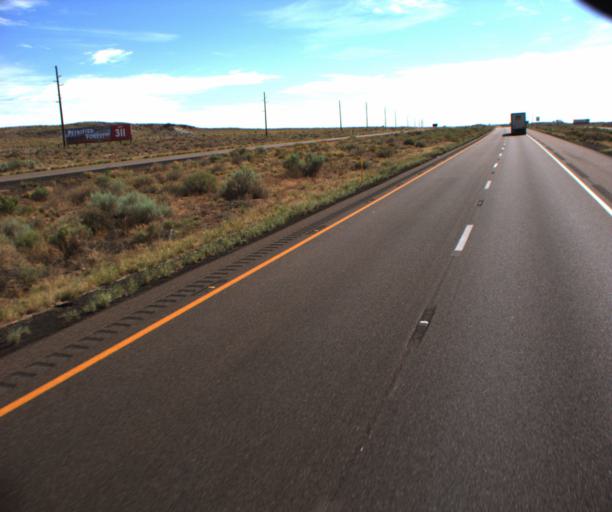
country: US
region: Arizona
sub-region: Navajo County
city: Holbrook
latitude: 35.0019
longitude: -109.8925
